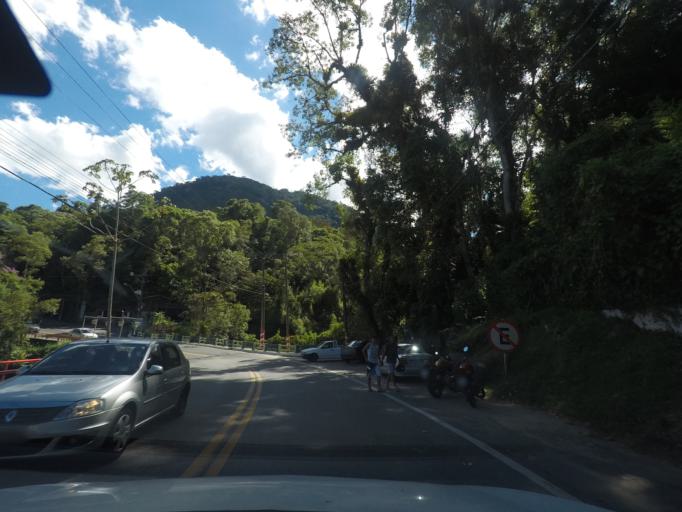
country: BR
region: Rio de Janeiro
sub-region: Teresopolis
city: Teresopolis
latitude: -22.4478
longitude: -42.9831
